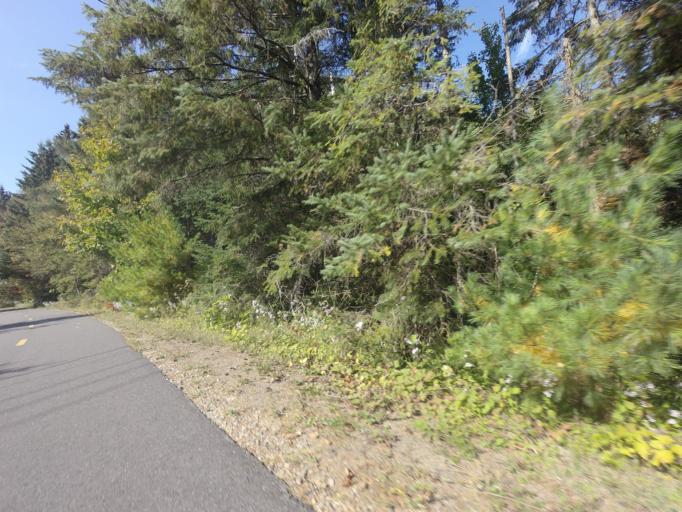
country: CA
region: Quebec
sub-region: Laurentides
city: Mont-Tremblant
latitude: 46.1128
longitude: -74.5092
